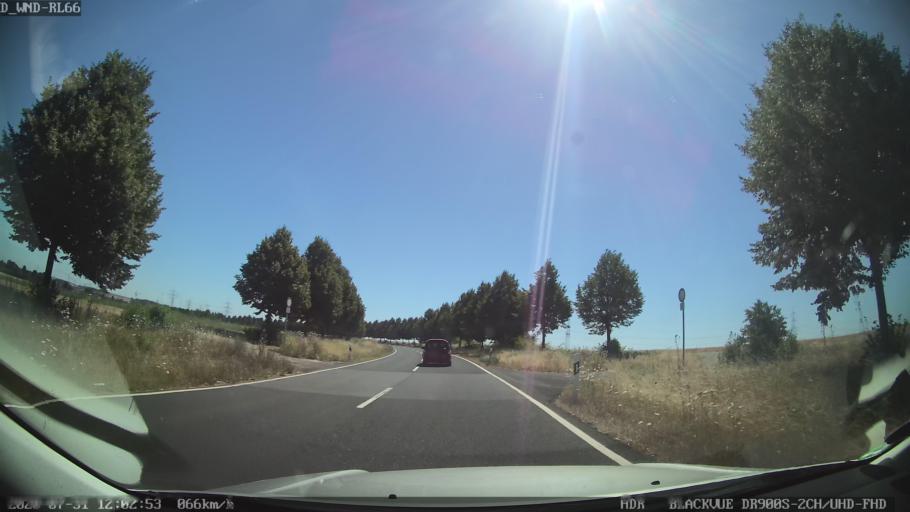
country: DE
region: Hesse
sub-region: Regierungsbezirk Darmstadt
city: Friedrichsdorf
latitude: 50.2182
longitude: 8.6706
